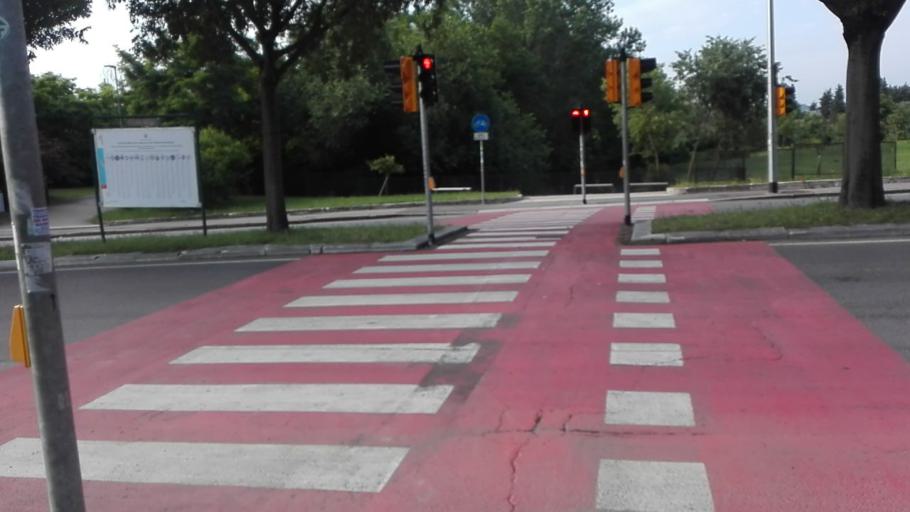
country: IT
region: Emilia-Romagna
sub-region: Provincia di Bologna
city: Bologna
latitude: 44.5172
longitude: 11.3333
